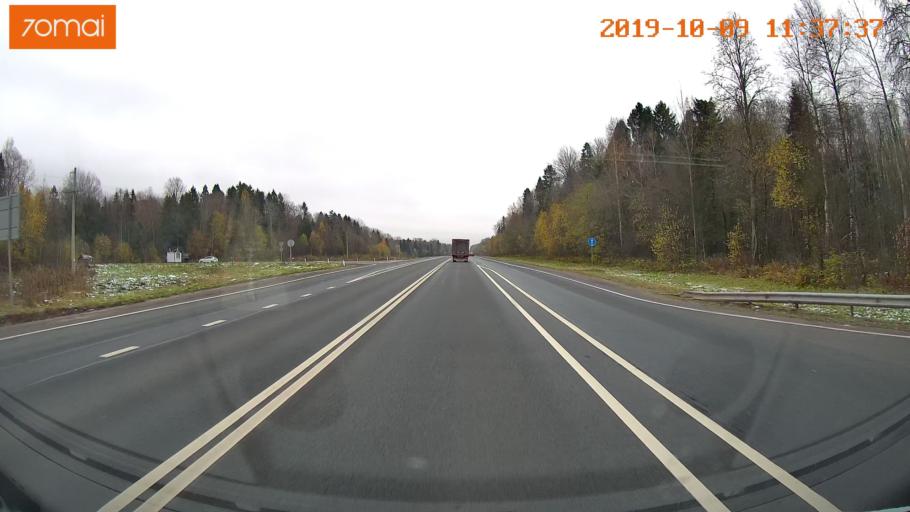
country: RU
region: Vologda
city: Gryazovets
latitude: 58.9773
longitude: 40.1481
